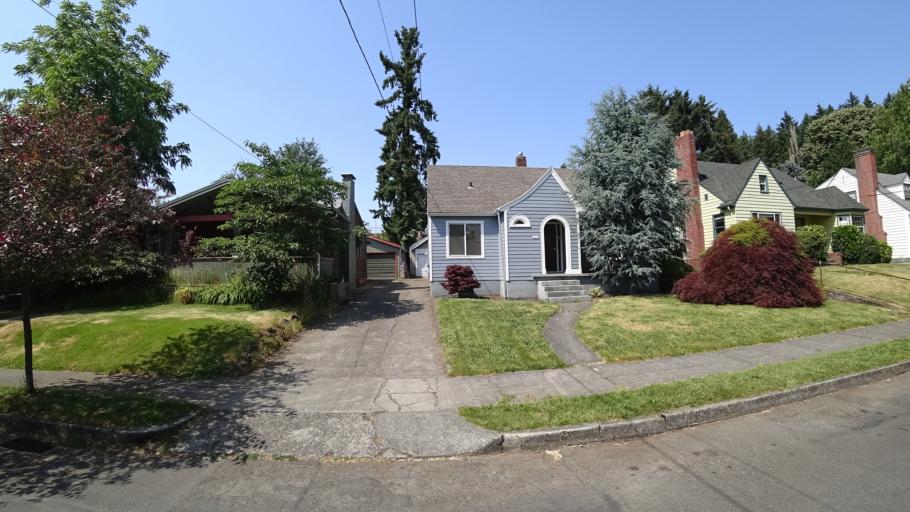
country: US
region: Oregon
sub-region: Multnomah County
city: Lents
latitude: 45.5094
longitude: -122.5995
